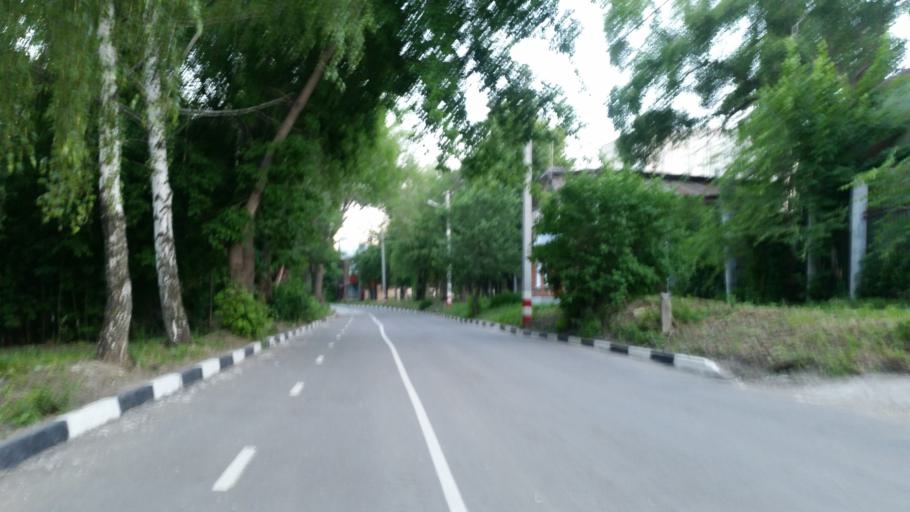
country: RU
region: Ulyanovsk
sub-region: Ulyanovskiy Rayon
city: Ulyanovsk
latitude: 54.3272
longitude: 48.4090
